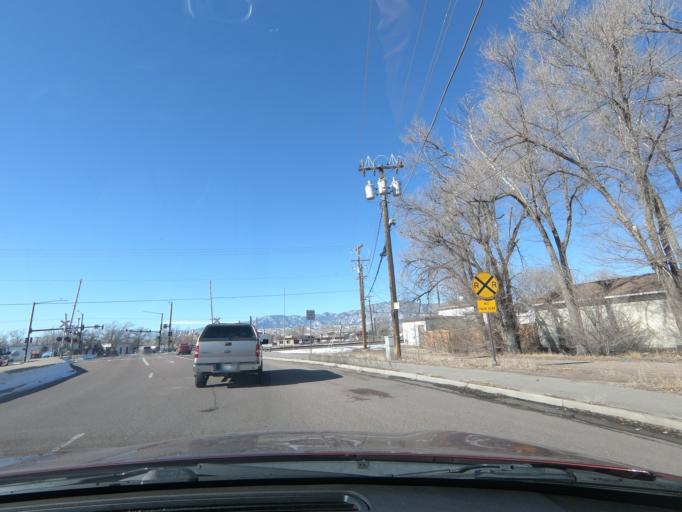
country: US
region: Colorado
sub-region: El Paso County
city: Security-Widefield
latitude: 38.7374
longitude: -104.7298
